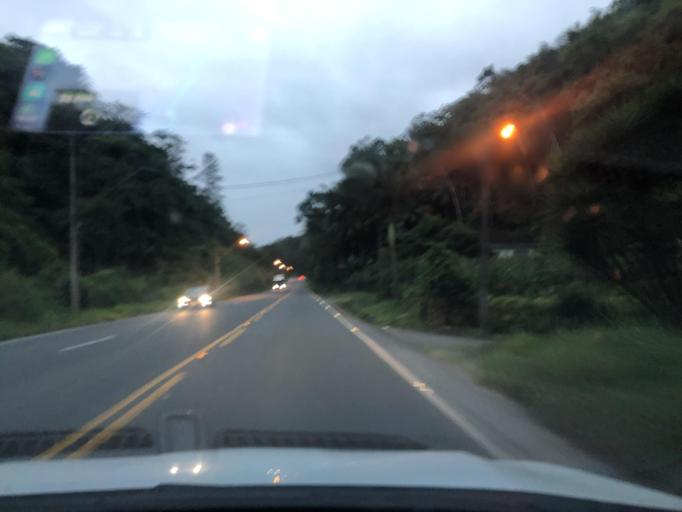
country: BR
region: Santa Catarina
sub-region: Pomerode
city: Pomerode
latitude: -26.7255
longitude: -49.0636
